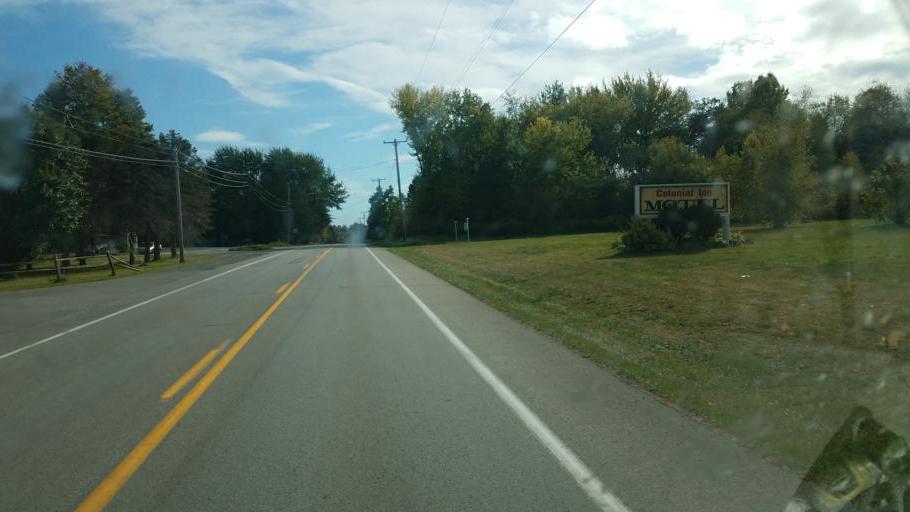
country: US
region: Pennsylvania
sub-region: Mercer County
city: Mercer
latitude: 41.2458
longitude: -80.2384
